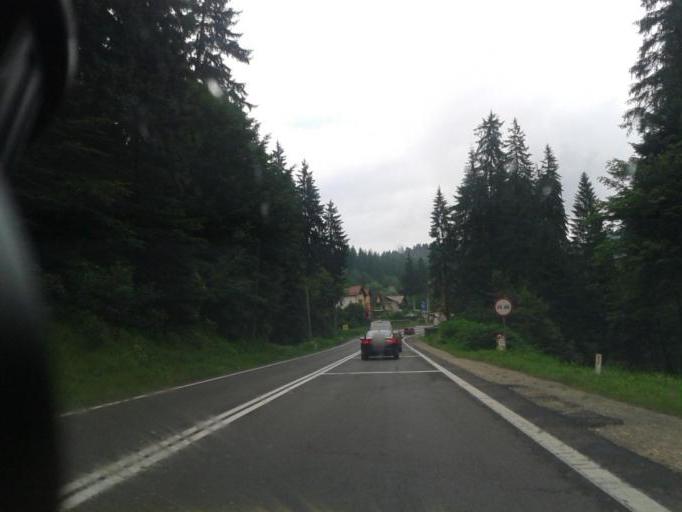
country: RO
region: Brasov
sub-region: Oras Predeal
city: Predeal
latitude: 45.5303
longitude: 25.5779
